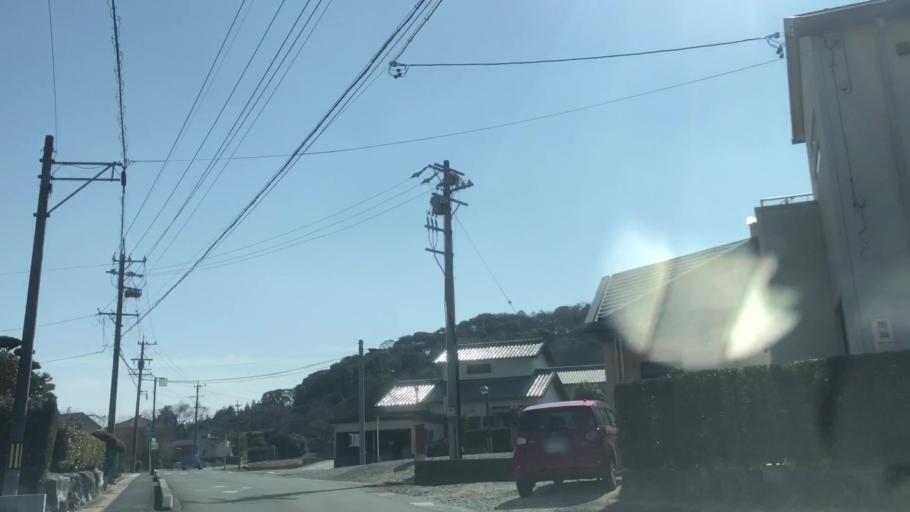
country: JP
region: Aichi
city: Tahara
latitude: 34.6693
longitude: 137.2541
